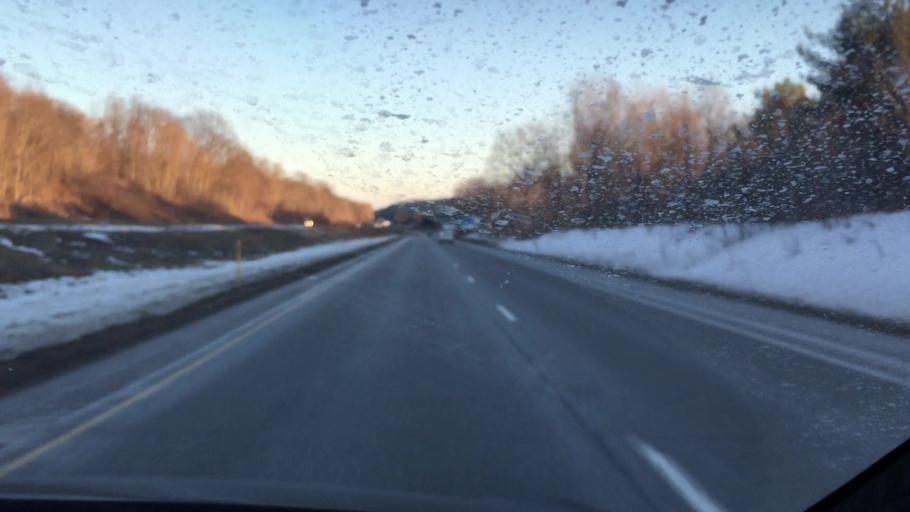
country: US
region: Pennsylvania
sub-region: Crawford County
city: Meadville
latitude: 41.6357
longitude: -80.1956
